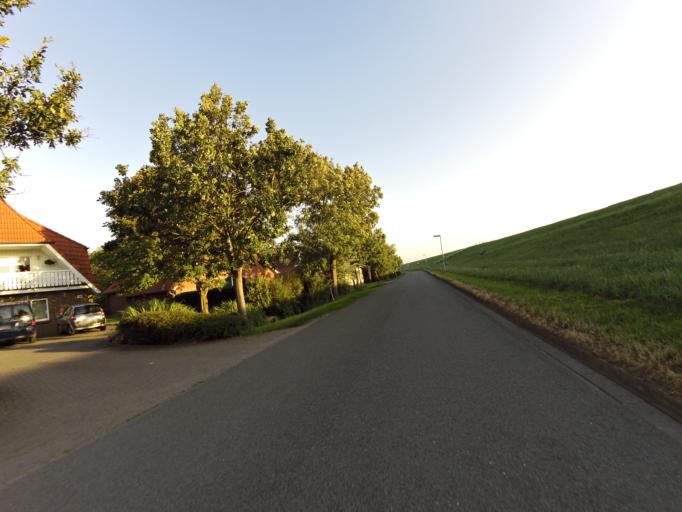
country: DE
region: Lower Saxony
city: Cappel
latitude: 53.7557
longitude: 8.5328
